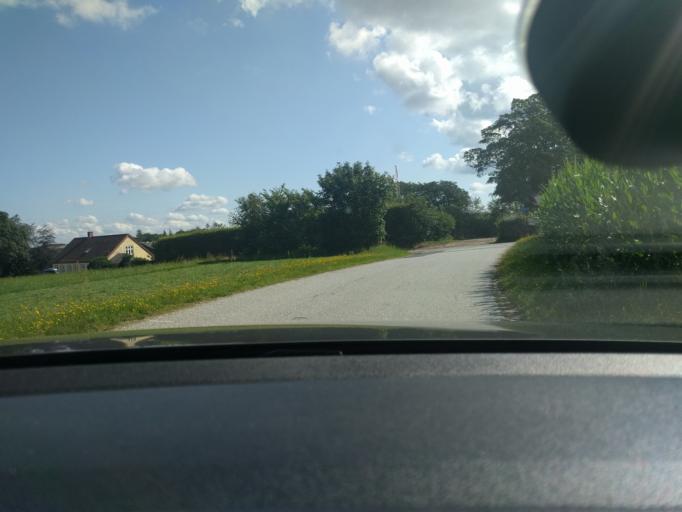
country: DK
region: Central Jutland
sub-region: Viborg Kommune
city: Viborg
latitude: 56.5060
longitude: 9.3042
